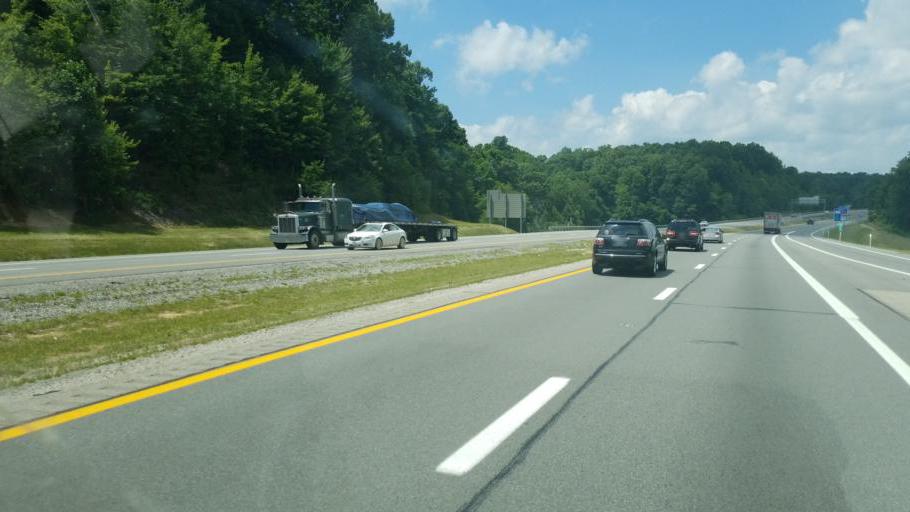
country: US
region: West Virginia
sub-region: Raleigh County
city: MacArthur
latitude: 37.7649
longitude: -81.2166
